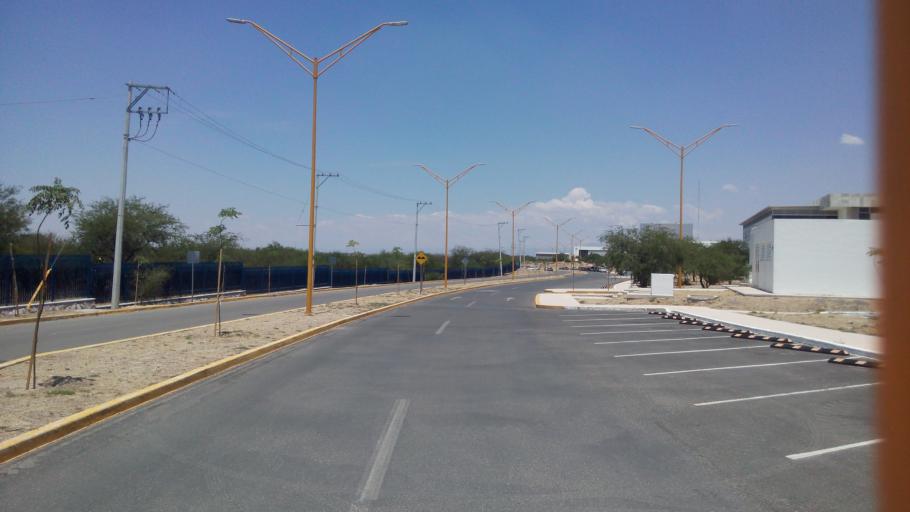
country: MX
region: Aguascalientes
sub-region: Aguascalientes
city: San Sebastian [Fraccionamiento]
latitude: 21.7926
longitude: -102.2883
